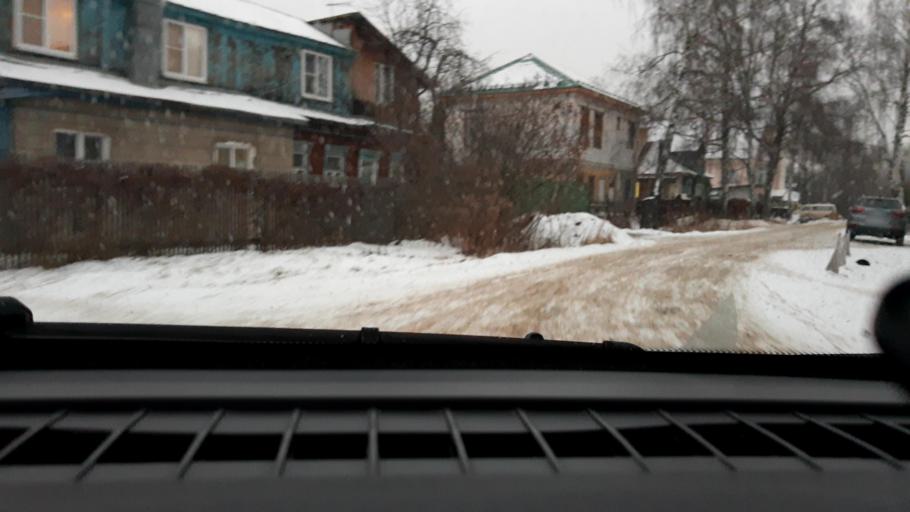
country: RU
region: Nizjnij Novgorod
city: Nizhniy Novgorod
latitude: 56.3021
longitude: 43.9085
